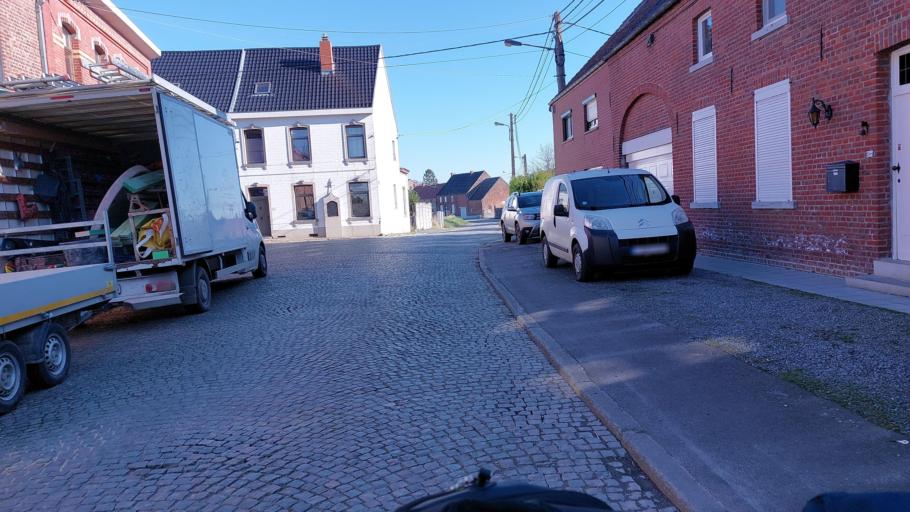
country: BE
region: Wallonia
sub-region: Province du Hainaut
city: Chievres
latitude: 50.5850
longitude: 3.7761
